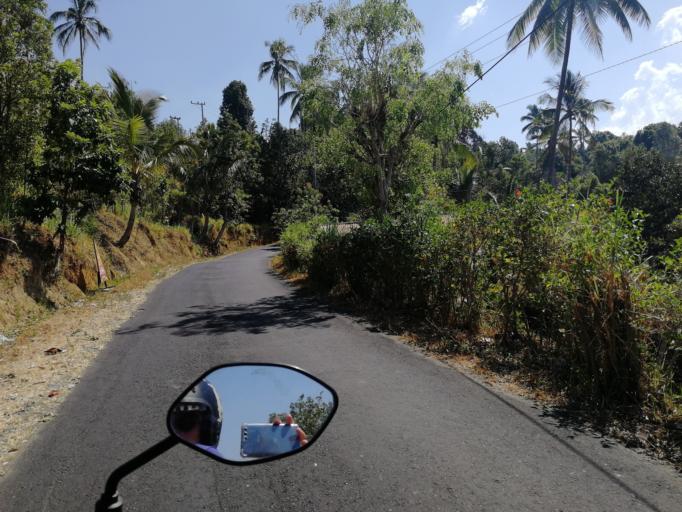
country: ID
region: Bali
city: Banjar Kedisan
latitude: -8.1548
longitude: 115.3075
